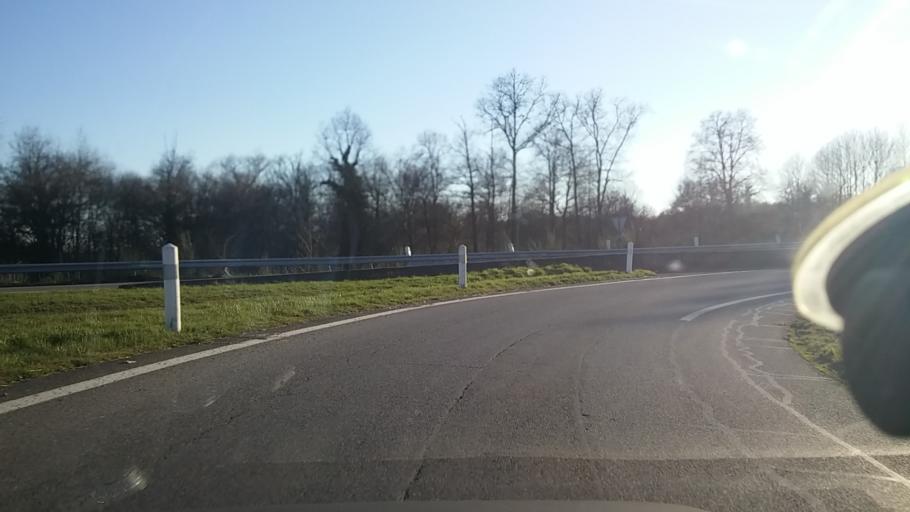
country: FR
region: Limousin
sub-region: Departement de la Haute-Vienne
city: Condat-sur-Vienne
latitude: 45.7799
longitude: 1.3044
